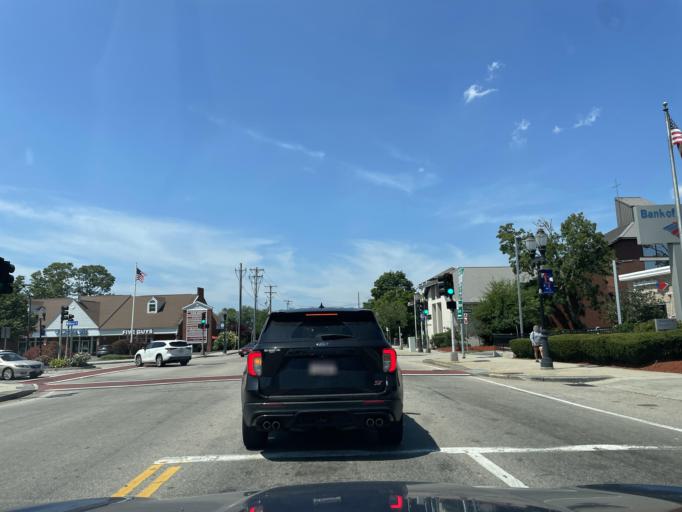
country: US
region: Massachusetts
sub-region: Norfolk County
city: Randolph
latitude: 42.1654
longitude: -71.0431
